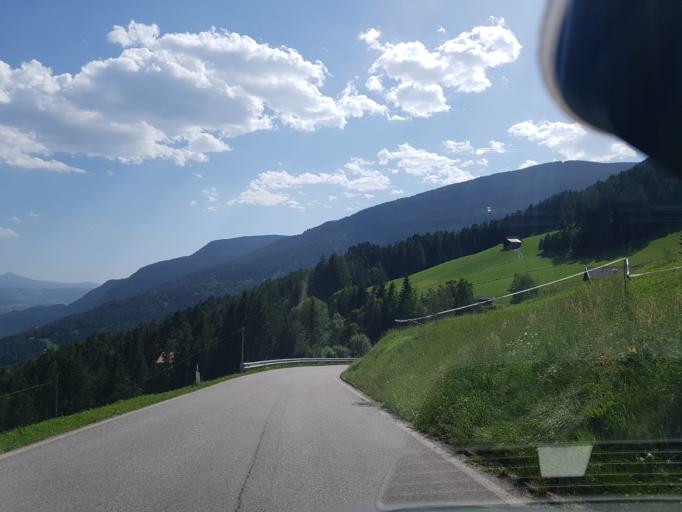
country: IT
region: Trentino-Alto Adige
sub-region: Bolzano
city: Villandro - Villanders
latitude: 46.6356
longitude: 11.5282
